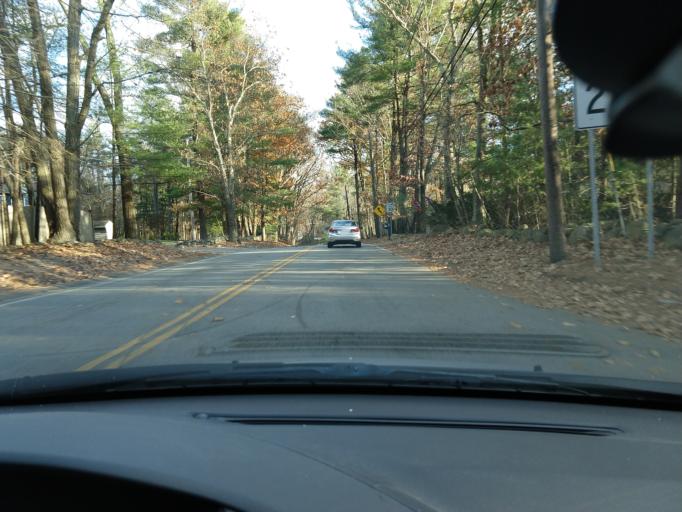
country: US
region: Massachusetts
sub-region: Middlesex County
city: Westford
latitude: 42.5523
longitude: -71.4379
